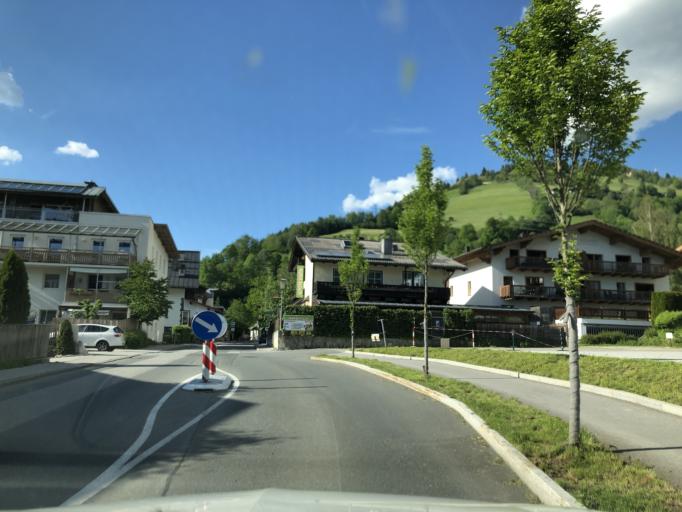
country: AT
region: Salzburg
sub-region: Politischer Bezirk Zell am See
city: Zell am See
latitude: 47.3282
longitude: 12.8168
